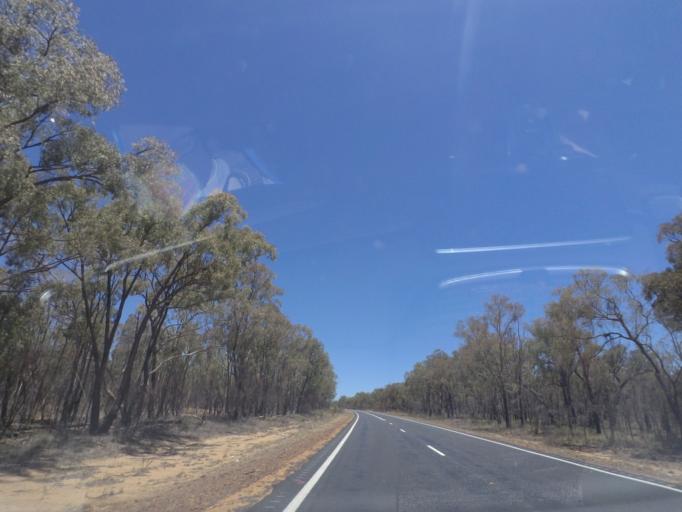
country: AU
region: New South Wales
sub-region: Warrumbungle Shire
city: Coonabarabran
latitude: -31.1769
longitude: 149.3573
